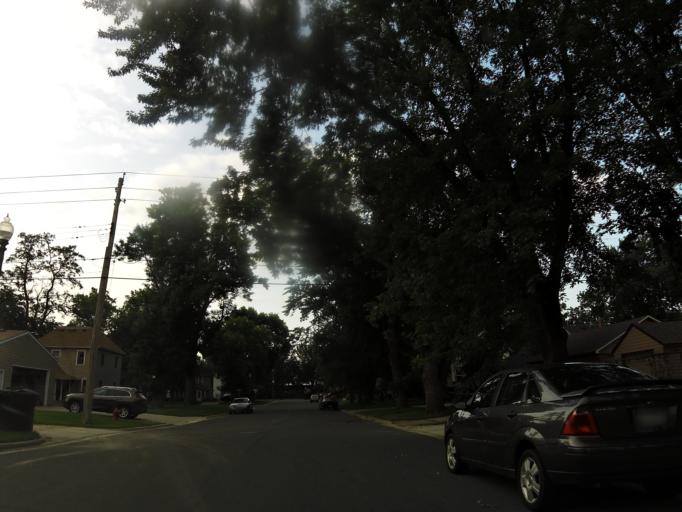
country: US
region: Minnesota
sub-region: Dakota County
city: Farmington
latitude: 44.6407
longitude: -93.1403
